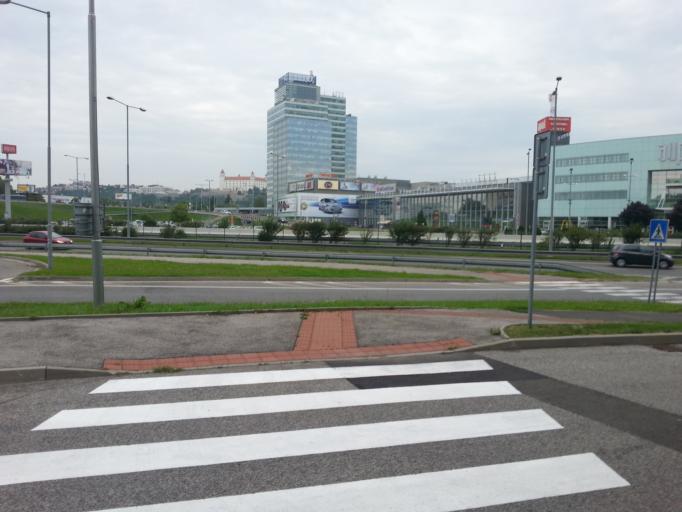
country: SK
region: Bratislavsky
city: Bratislava
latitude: 48.1311
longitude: 17.1070
